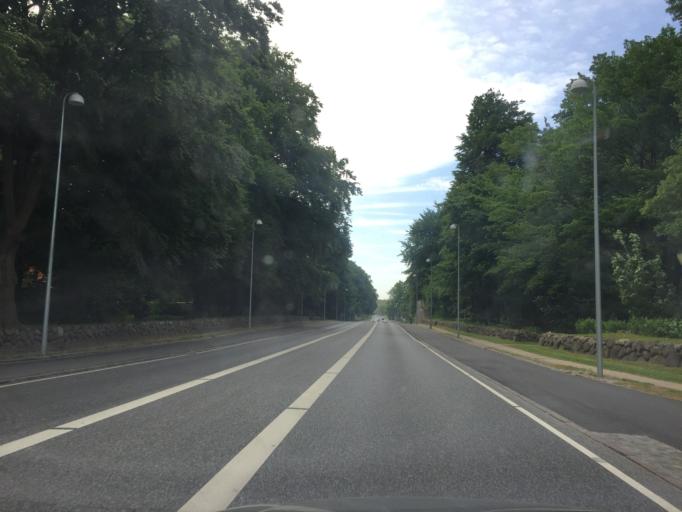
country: DK
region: Capital Region
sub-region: Lyngby-Tarbaek Kommune
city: Kongens Lyngby
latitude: 55.7786
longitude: 12.4942
